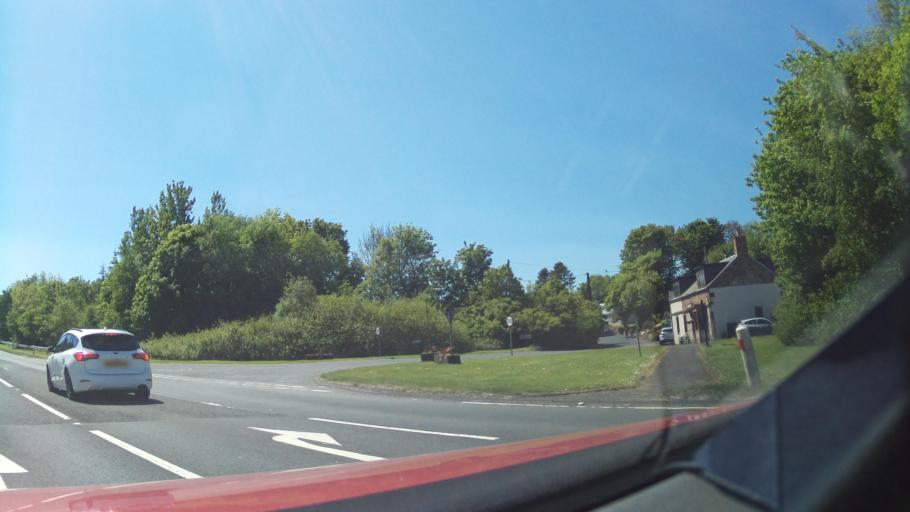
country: GB
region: Scotland
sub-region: The Scottish Borders
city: Selkirk
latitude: 55.4930
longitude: -2.8353
